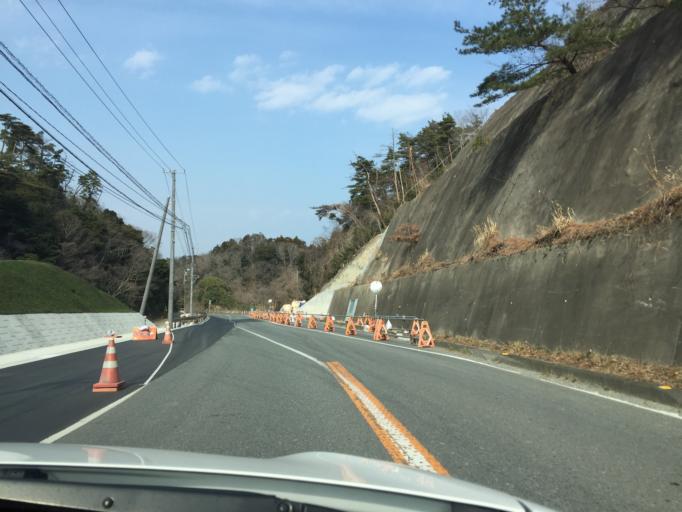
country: JP
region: Fukushima
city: Iwaki
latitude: 37.0007
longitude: 140.9674
